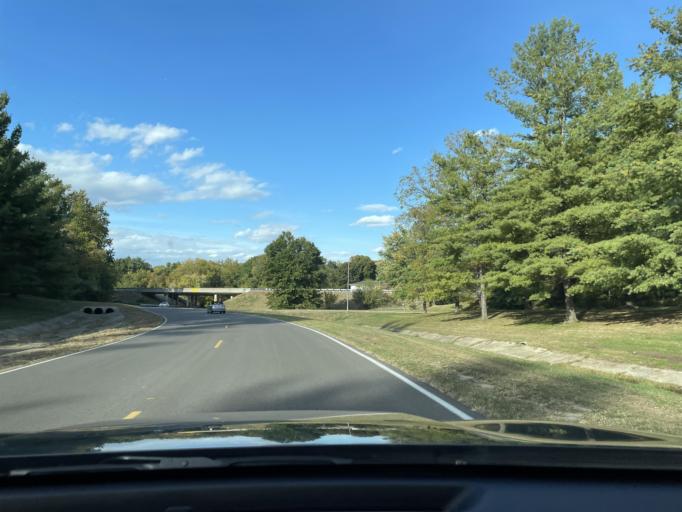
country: US
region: Kansas
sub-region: Doniphan County
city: Elwood
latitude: 39.7259
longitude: -94.8440
